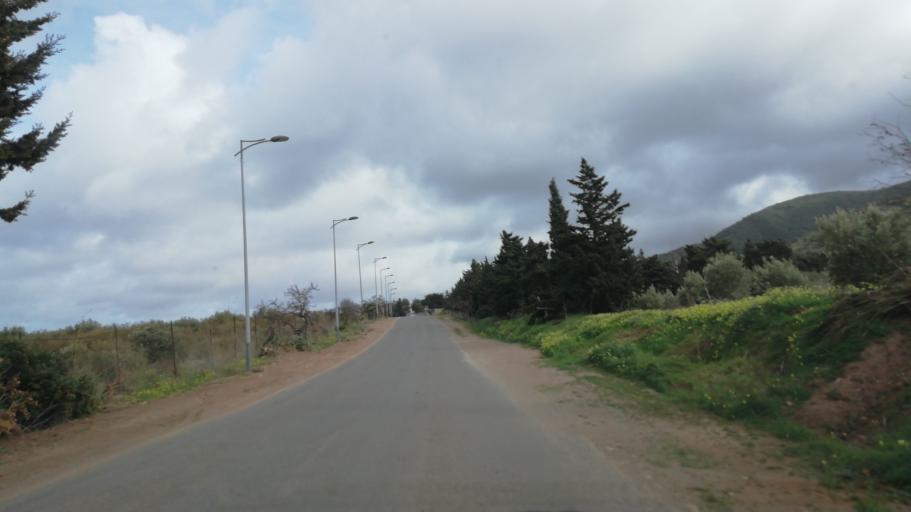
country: DZ
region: Oran
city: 'Ain el Turk
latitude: 35.6958
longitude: -0.8544
